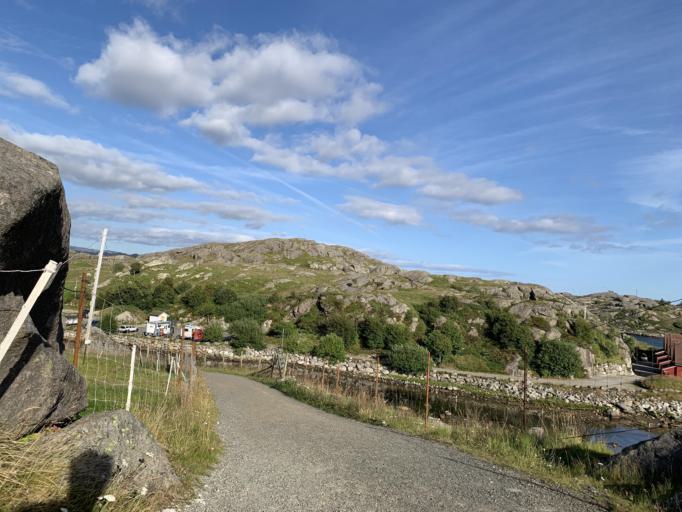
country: NO
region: Rogaland
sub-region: Eigersund
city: Egersund
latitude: 58.4414
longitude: 5.8842
